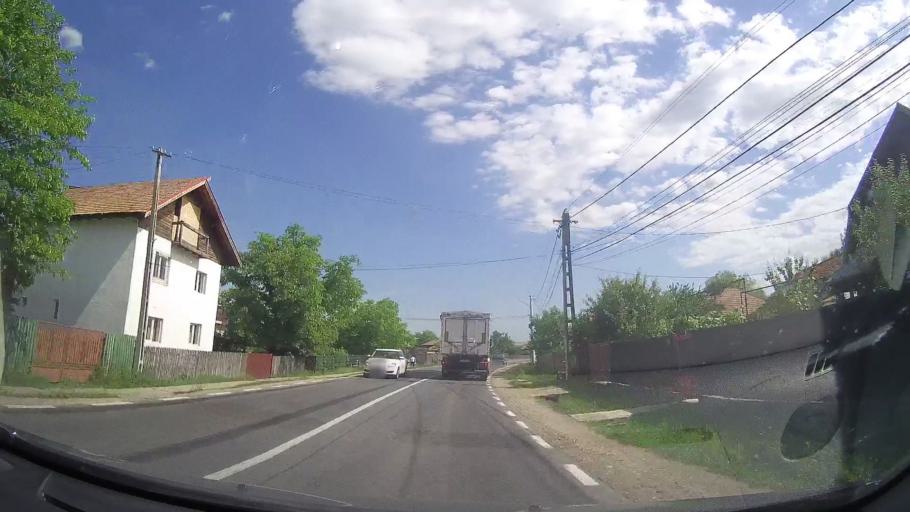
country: RO
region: Prahova
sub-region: Comuna Maneciu-Ungureni
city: Gheaba
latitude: 45.2969
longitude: 25.9999
